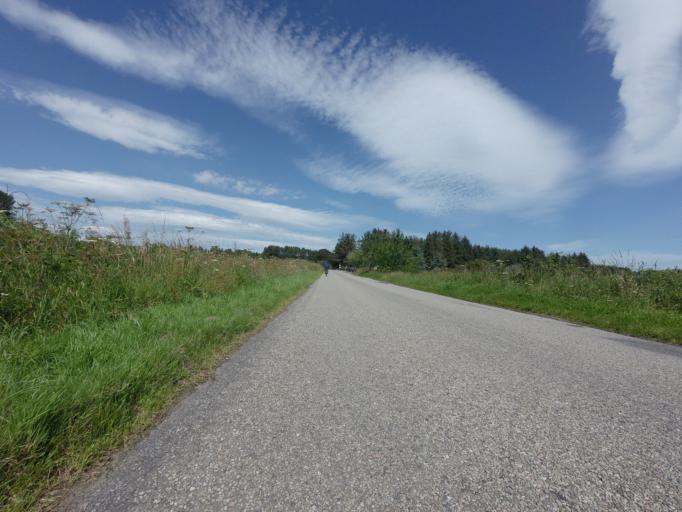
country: GB
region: Scotland
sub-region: Highland
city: Inverness
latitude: 57.5300
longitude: -4.3201
